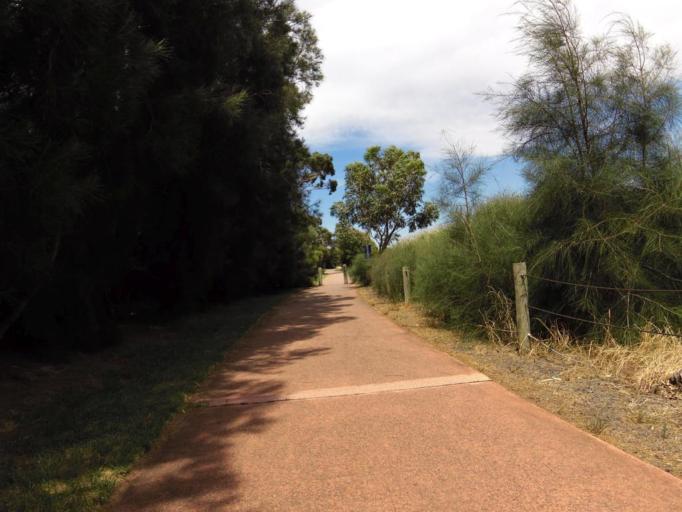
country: AU
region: Victoria
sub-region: Hobsons Bay
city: Seaholme
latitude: -37.8585
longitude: 144.8421
